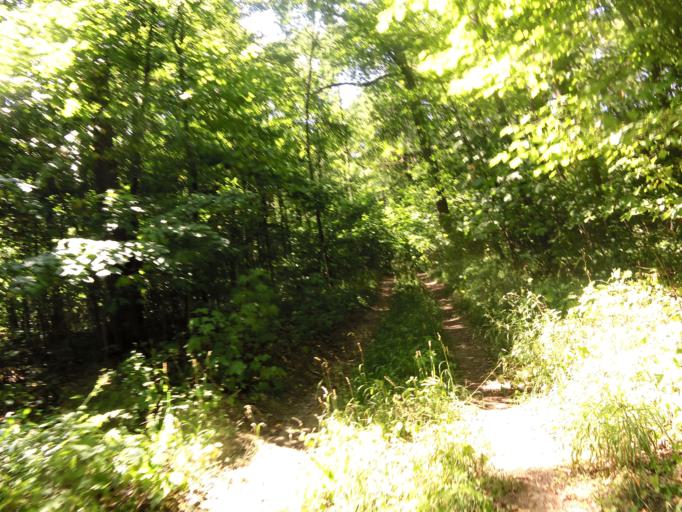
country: DE
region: Bavaria
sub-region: Regierungsbezirk Unterfranken
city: Rimpar
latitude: 49.8266
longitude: 9.9530
